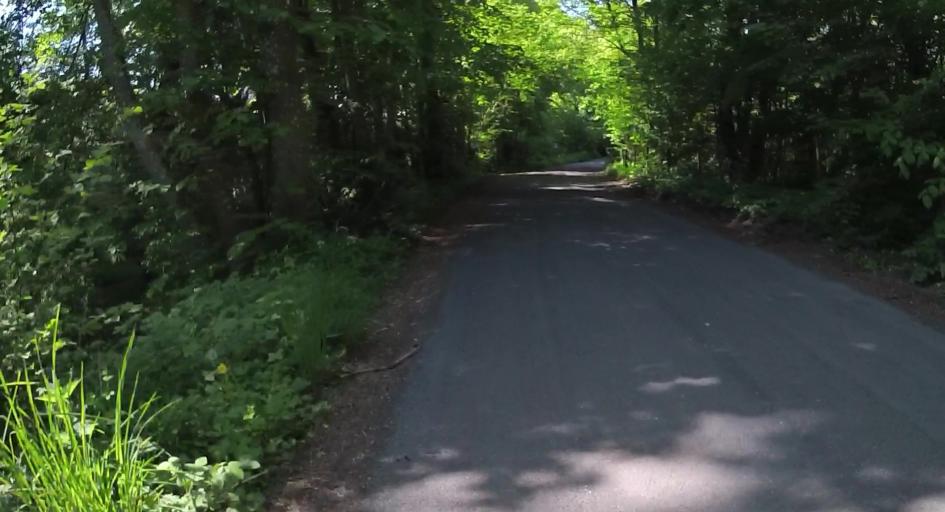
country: GB
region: England
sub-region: Hampshire
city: Kings Worthy
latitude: 51.0822
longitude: -1.1987
